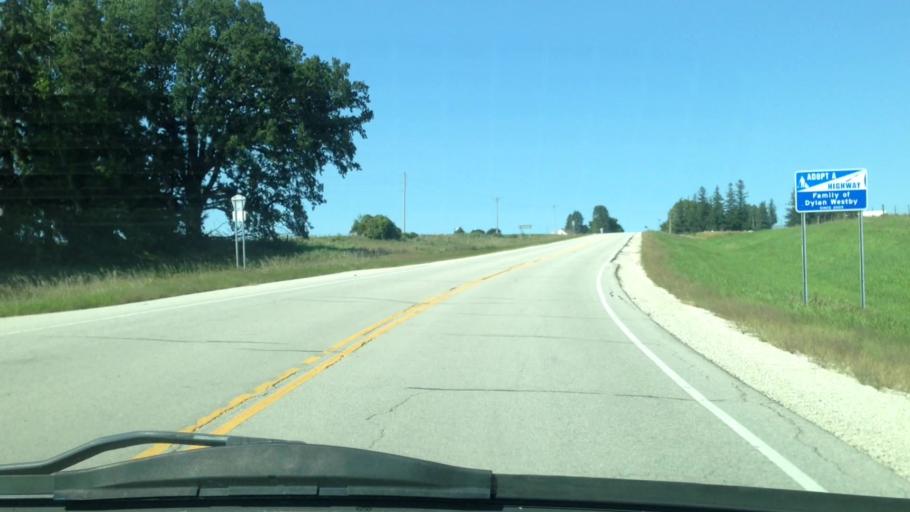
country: US
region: Minnesota
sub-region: Houston County
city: Spring Grove
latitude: 43.6036
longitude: -91.7900
